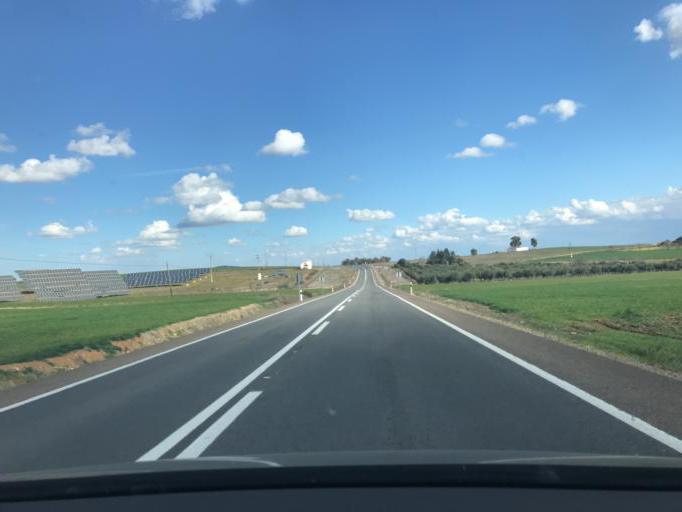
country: ES
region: Extremadura
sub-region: Provincia de Badajoz
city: Granja de Torrehermosa
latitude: 38.2980
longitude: -5.6348
